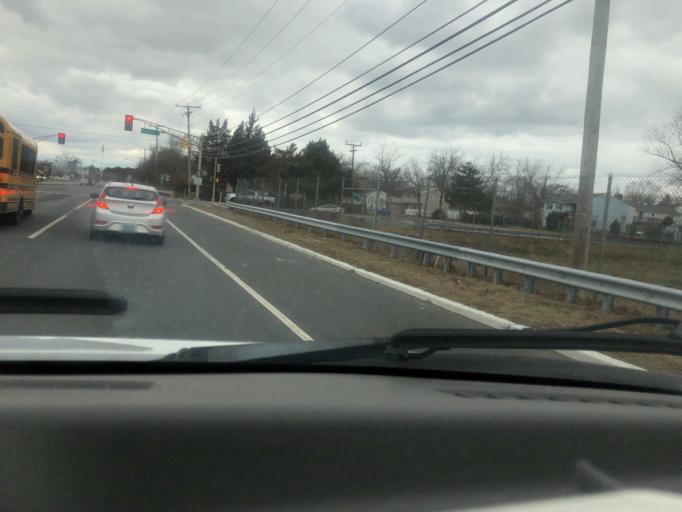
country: US
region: New Jersey
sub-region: Ocean County
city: Holiday City South
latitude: 39.9766
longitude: -74.2449
